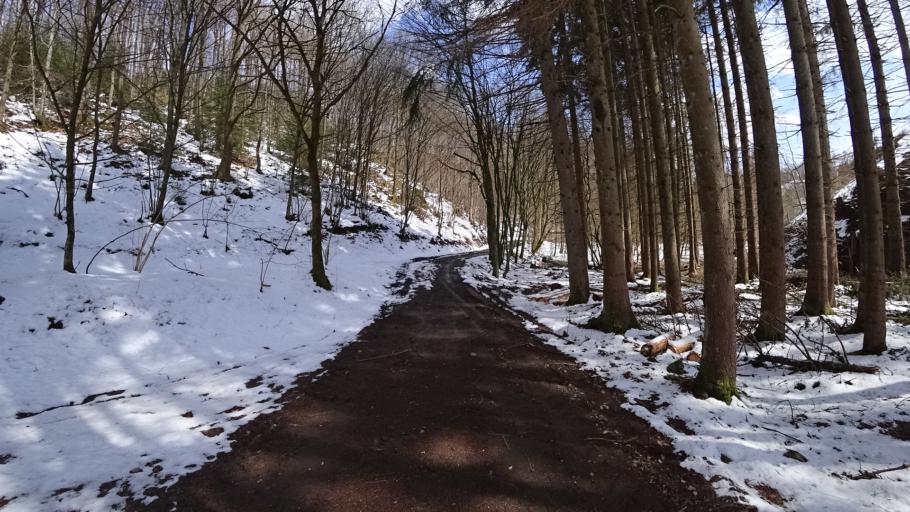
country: DE
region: Rheinland-Pfalz
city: Kausen
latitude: 50.7371
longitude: 7.8599
